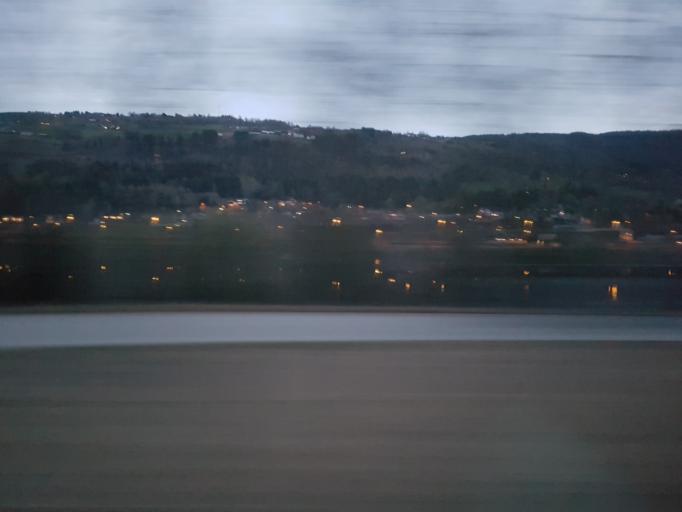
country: NO
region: Oppland
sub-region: Oyer
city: Tretten
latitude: 61.2644
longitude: 10.4057
